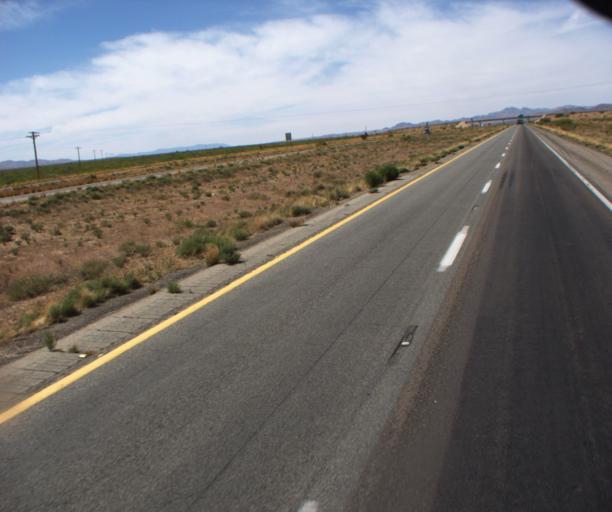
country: US
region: Arizona
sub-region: Cochise County
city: Willcox
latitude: 32.3258
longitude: -109.5069
